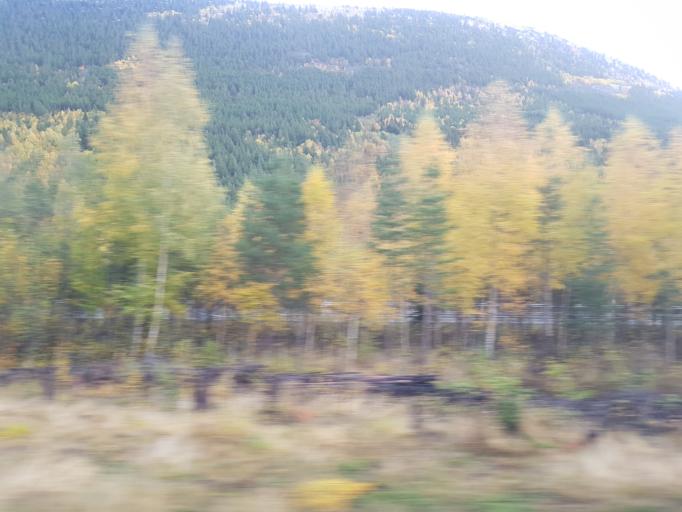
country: NO
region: Oppland
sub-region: Dovre
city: Dovre
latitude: 61.9282
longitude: 9.3223
